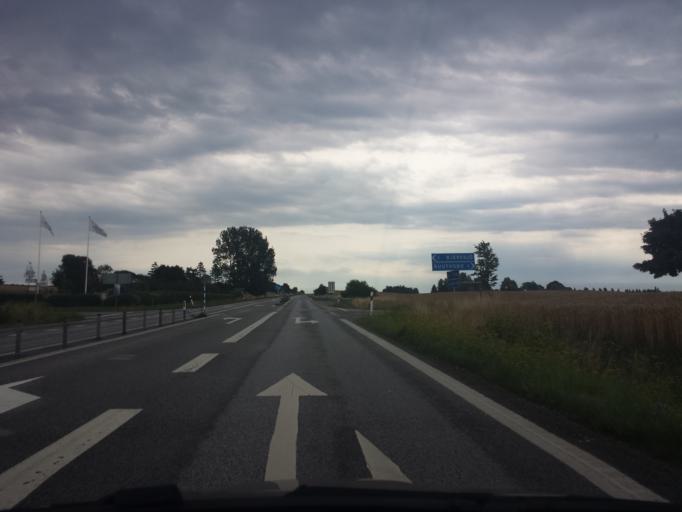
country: SE
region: Skane
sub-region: Ystads Kommun
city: Ystad
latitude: 55.4565
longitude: 13.7432
